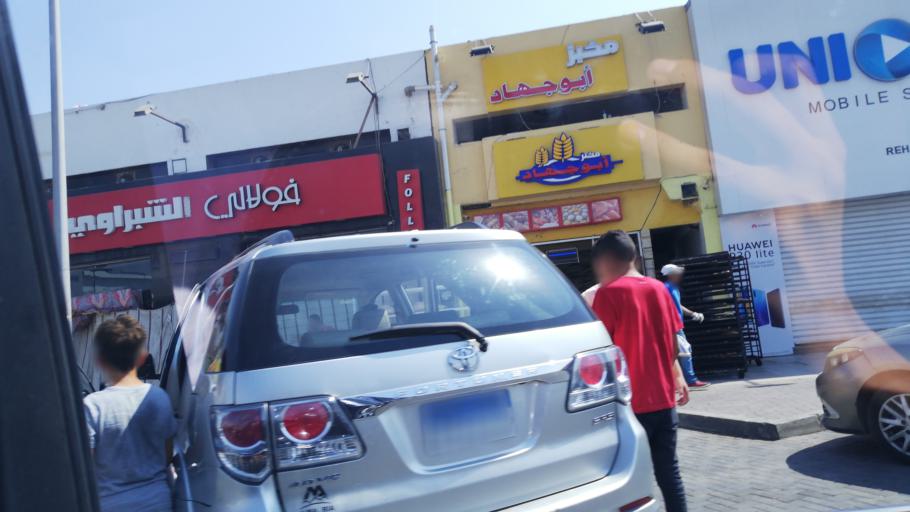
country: EG
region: Muhafazat al Qalyubiyah
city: Al Khankah
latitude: 30.0559
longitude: 31.4922
